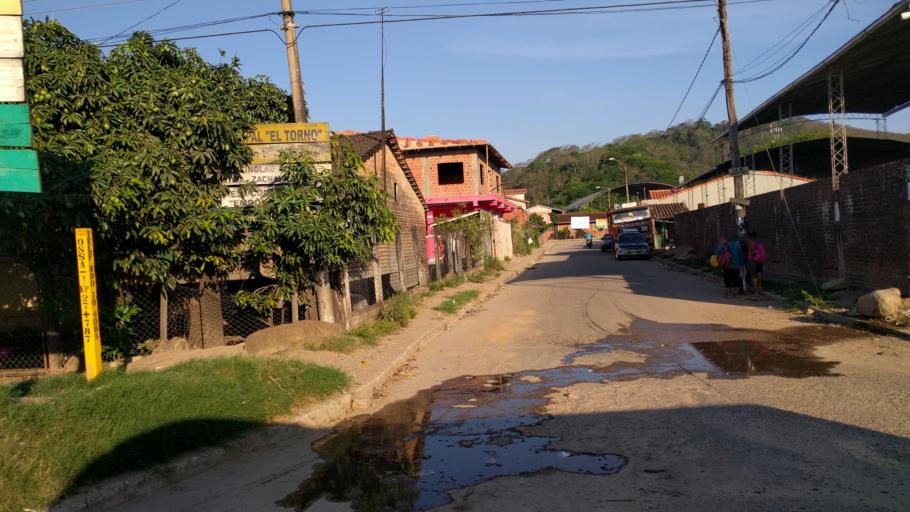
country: BO
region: Santa Cruz
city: Santiago del Torno
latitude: -17.9986
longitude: -63.3861
